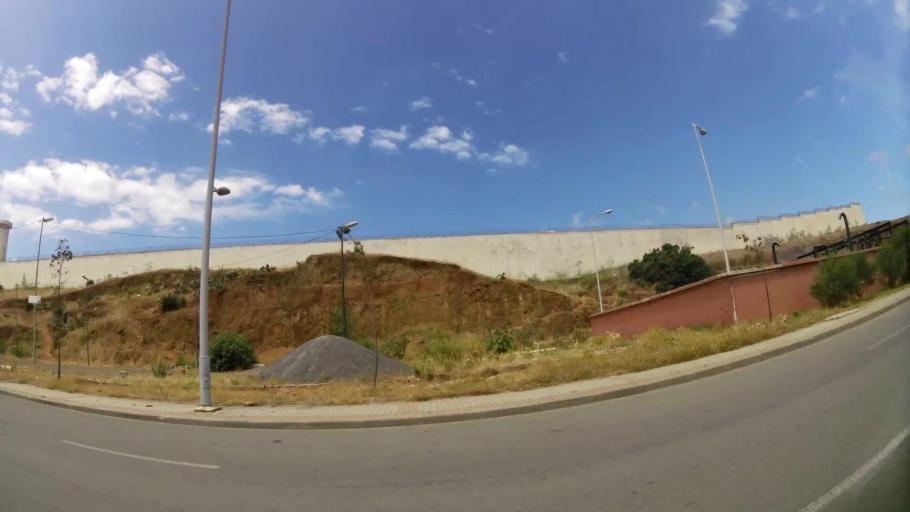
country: MA
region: Gharb-Chrarda-Beni Hssen
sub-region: Kenitra Province
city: Kenitra
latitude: 34.2737
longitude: -6.5914
